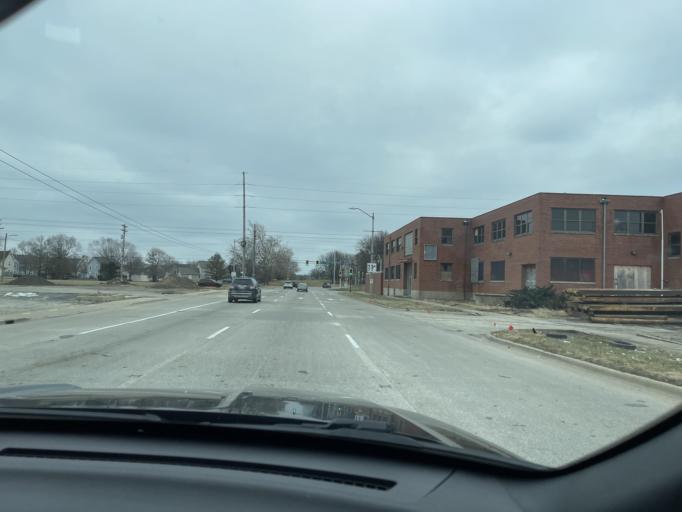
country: US
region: Illinois
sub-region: Sangamon County
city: Springfield
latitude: 39.8038
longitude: -89.6420
